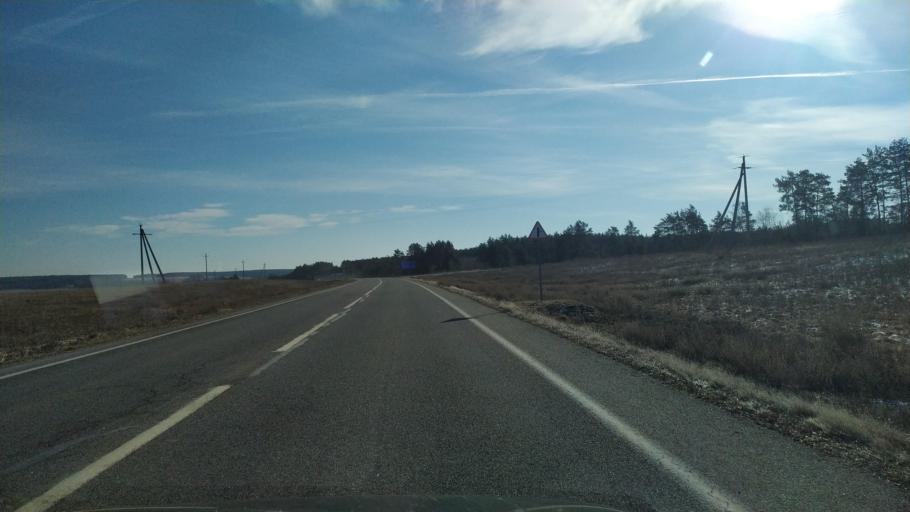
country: BY
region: Brest
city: Kamyanyets
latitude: 52.4041
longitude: 23.8640
